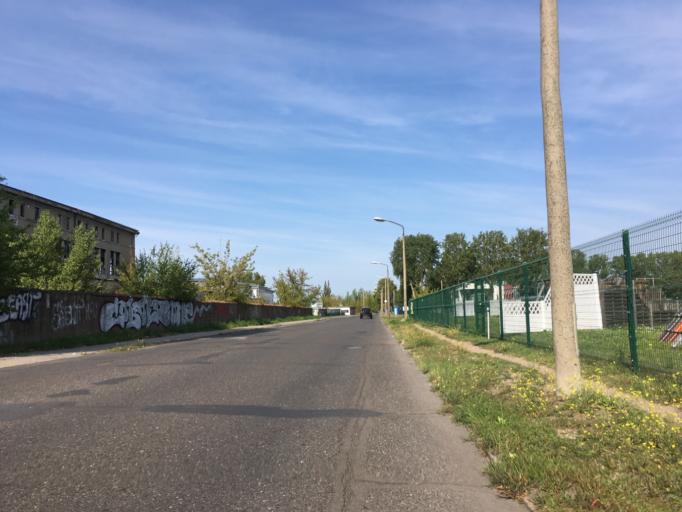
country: DE
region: Brandenburg
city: Eisenhuettenstadt
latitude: 52.1443
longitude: 14.6501
